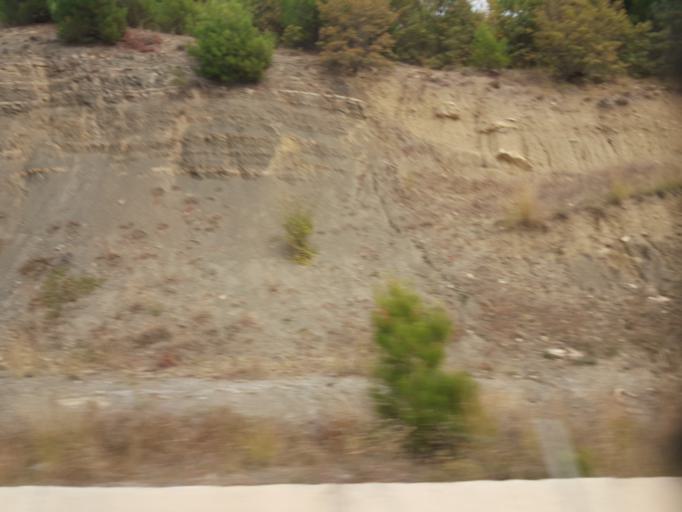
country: TR
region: Sinop
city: Duragan
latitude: 41.4656
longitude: 35.0420
